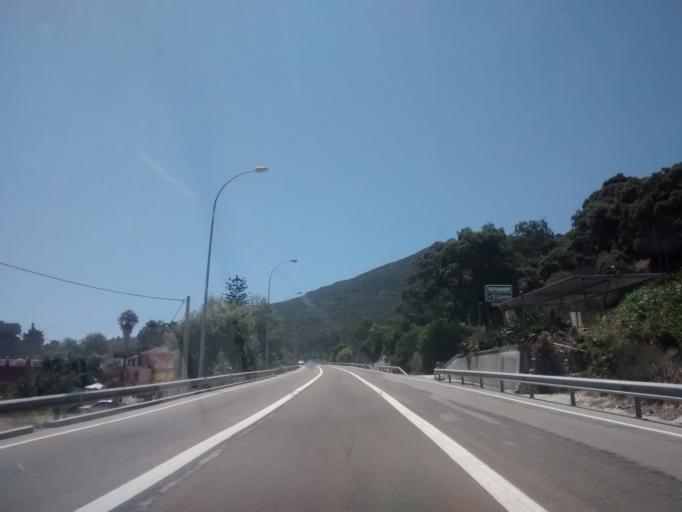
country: ES
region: Andalusia
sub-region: Provincia de Cadiz
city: Algeciras
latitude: 36.0833
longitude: -5.5000
